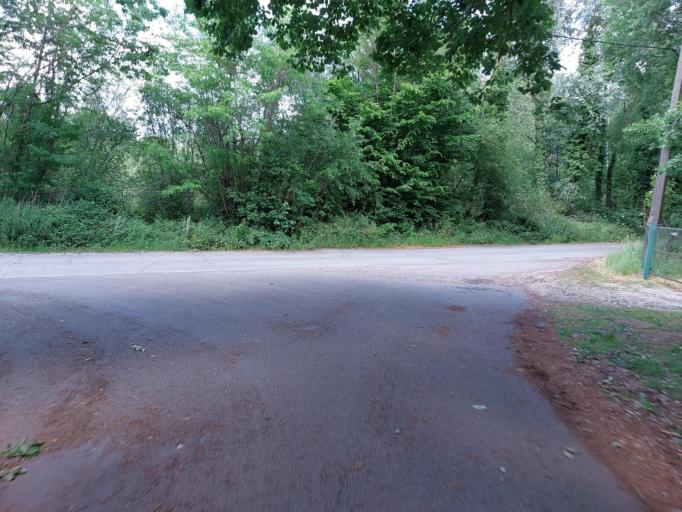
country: BE
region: Wallonia
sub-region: Province du Hainaut
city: Boussu
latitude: 50.4904
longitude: 3.7745
